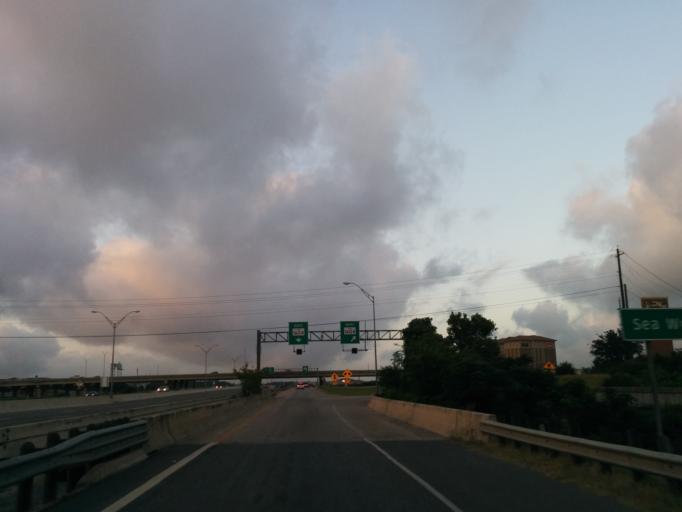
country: US
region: Texas
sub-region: Bexar County
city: Shavano Park
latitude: 29.5938
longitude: -98.5991
